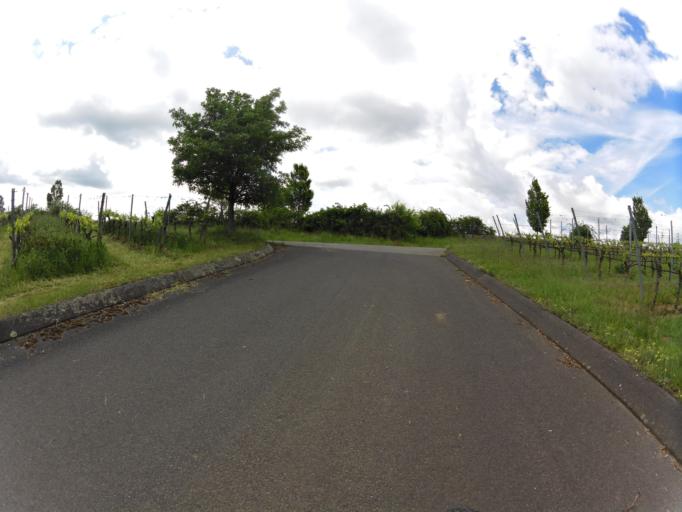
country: DE
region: Bavaria
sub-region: Regierungsbezirk Unterfranken
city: Sommerach
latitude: 49.8386
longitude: 10.2048
